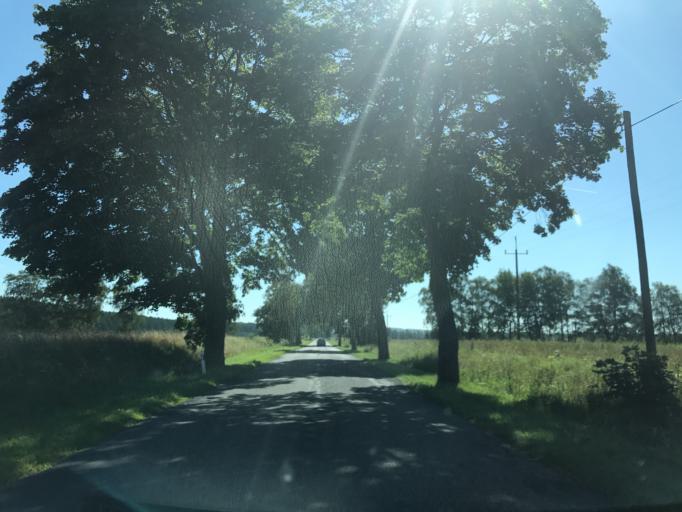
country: PL
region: Pomeranian Voivodeship
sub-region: Powiat bytowski
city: Czarna Dabrowka
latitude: 54.3610
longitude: 17.5318
